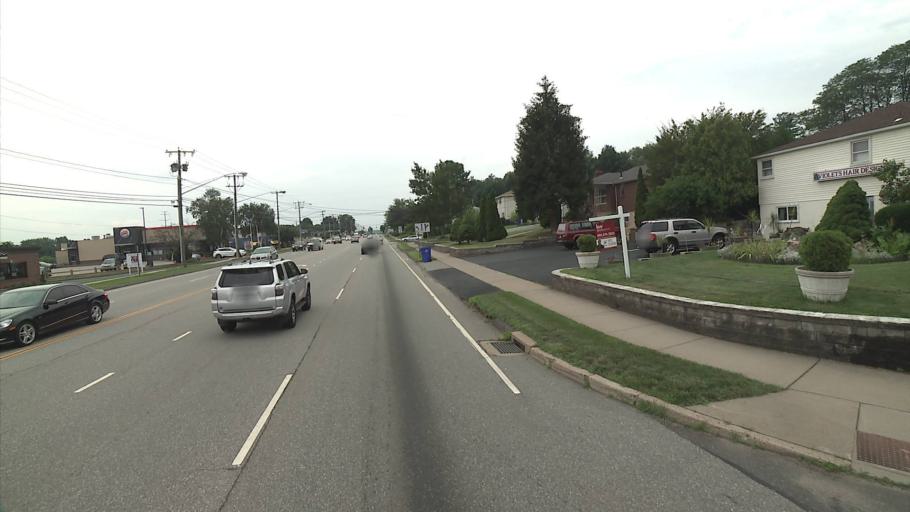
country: US
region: Connecticut
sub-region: Hartford County
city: Wethersfield
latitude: 41.7004
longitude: -72.6594
